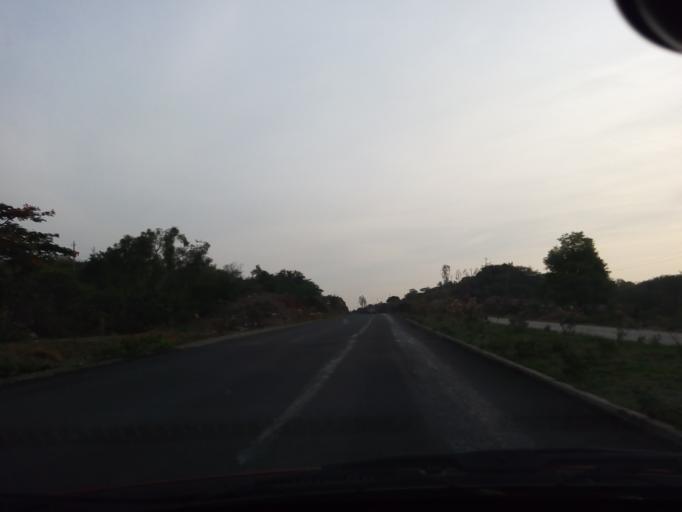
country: IN
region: Karnataka
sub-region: Chikkaballapur
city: Chik Ballapur
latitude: 13.5516
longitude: 77.7760
